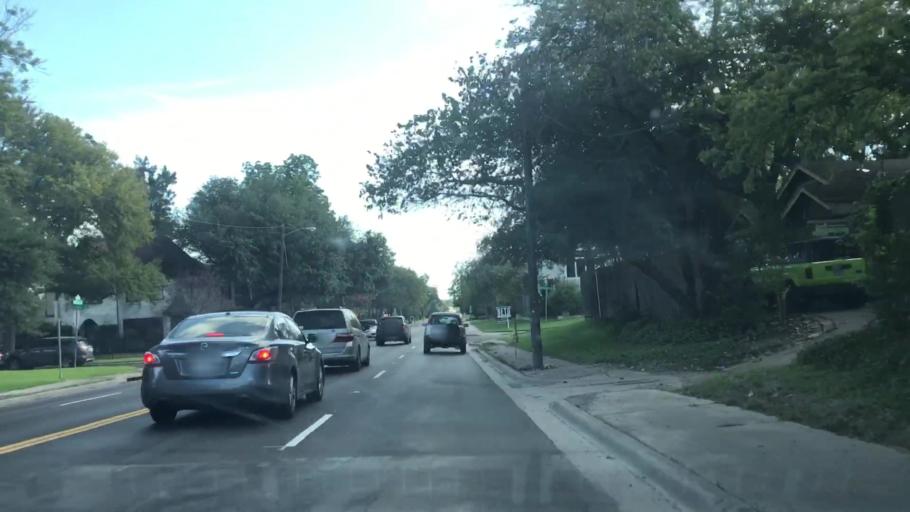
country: US
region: Texas
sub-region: Dallas County
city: Highland Park
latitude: 32.8215
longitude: -96.7617
